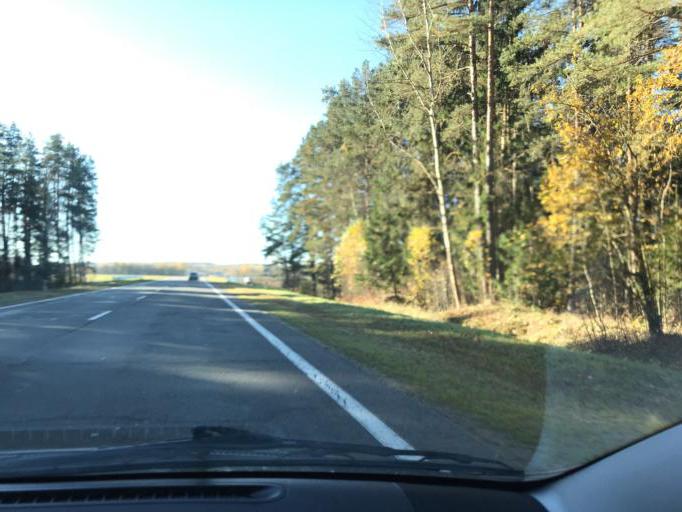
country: BY
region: Vitebsk
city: Syanno
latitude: 55.0534
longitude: 29.5215
